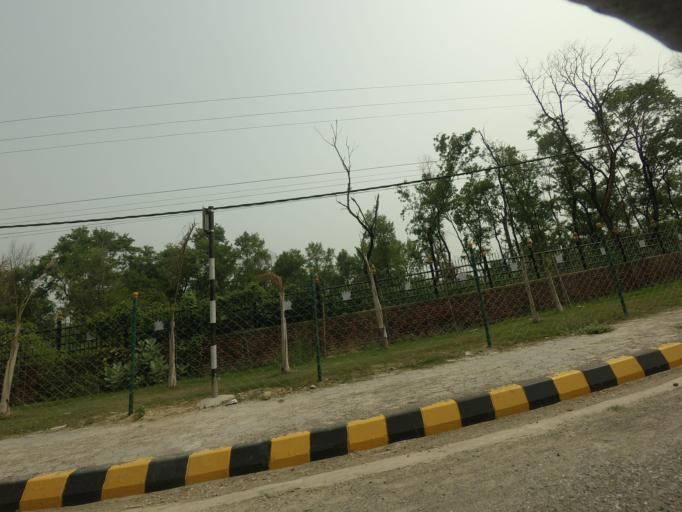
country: IN
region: Uttar Pradesh
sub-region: Maharajganj
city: Nautanwa
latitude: 27.4916
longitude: 83.2699
